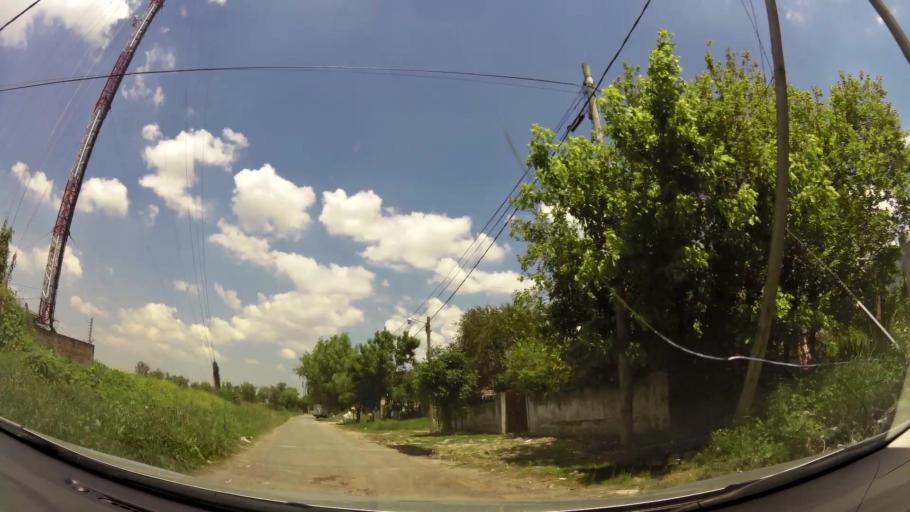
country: AR
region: Buenos Aires
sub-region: Partido de Tigre
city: Tigre
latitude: -34.4032
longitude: -58.6026
